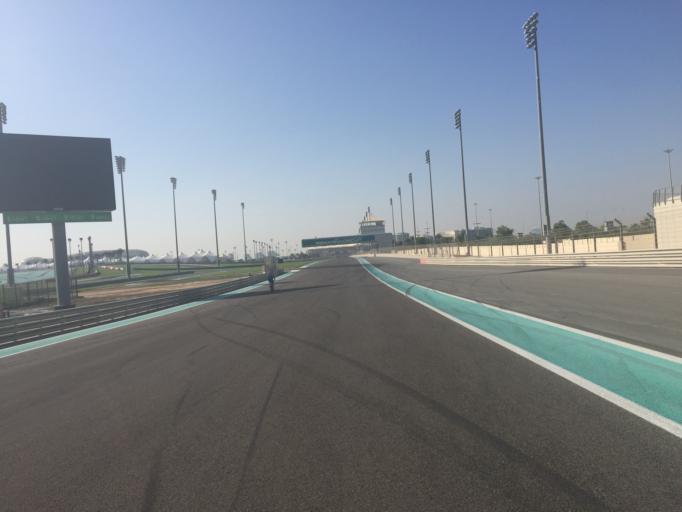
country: AE
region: Abu Dhabi
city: Abu Dhabi
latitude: 24.4781
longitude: 54.6050
